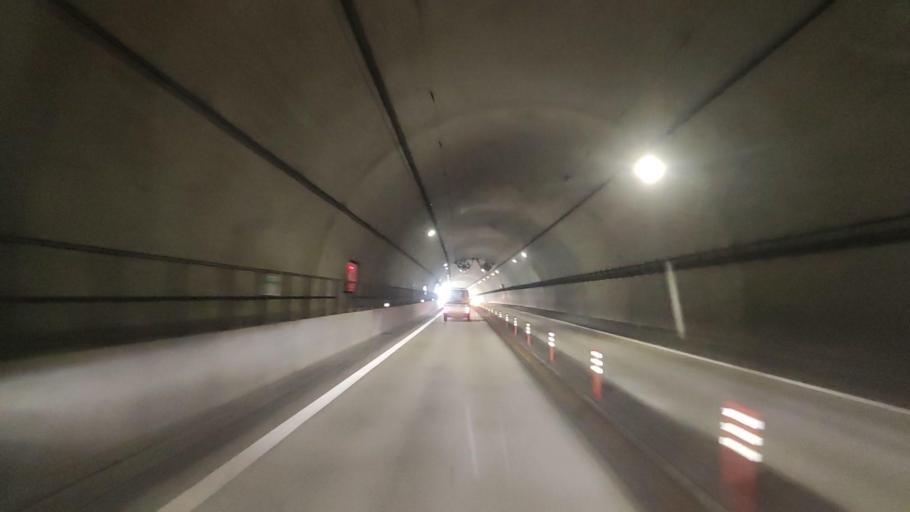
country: JP
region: Wakayama
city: Tanabe
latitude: 33.6301
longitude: 135.4144
